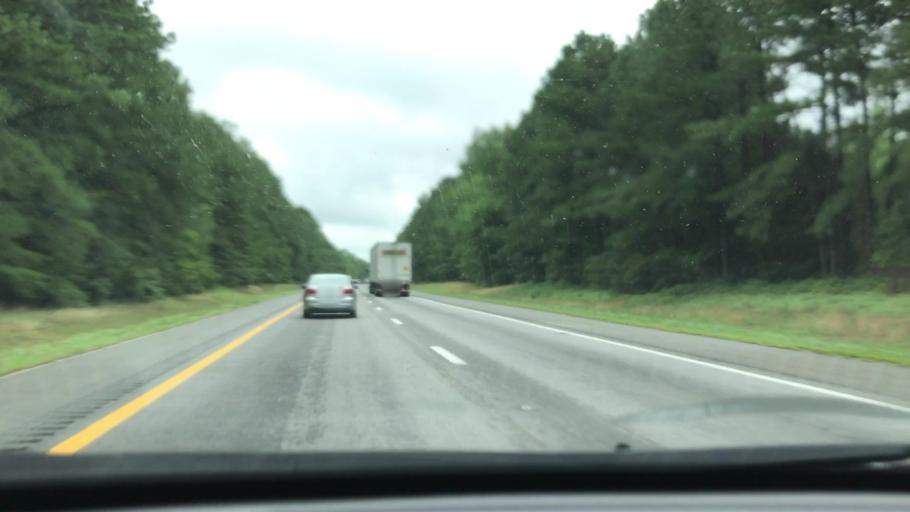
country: US
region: Virginia
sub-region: City of Emporia
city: Emporia
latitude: 36.7923
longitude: -77.4613
